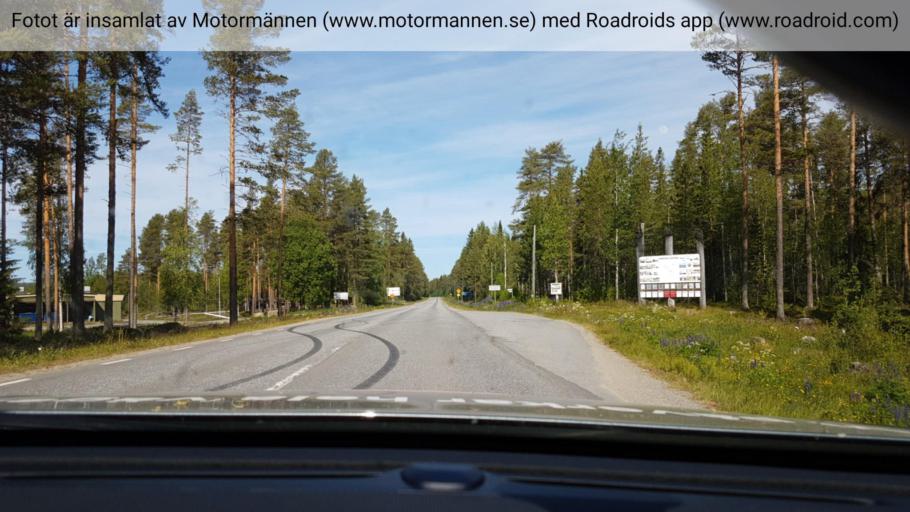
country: SE
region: Vaesterbotten
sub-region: Dorotea Kommun
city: Dorotea
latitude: 64.2595
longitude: 16.3767
